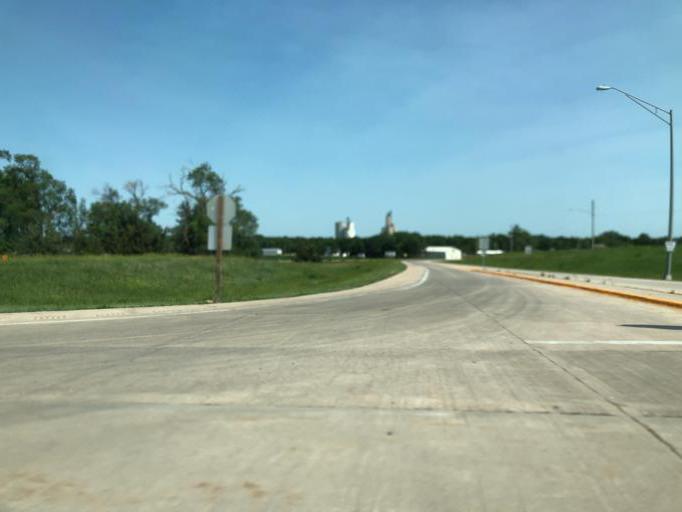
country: US
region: Nebraska
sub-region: York County
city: York
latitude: 40.7490
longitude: -97.6004
